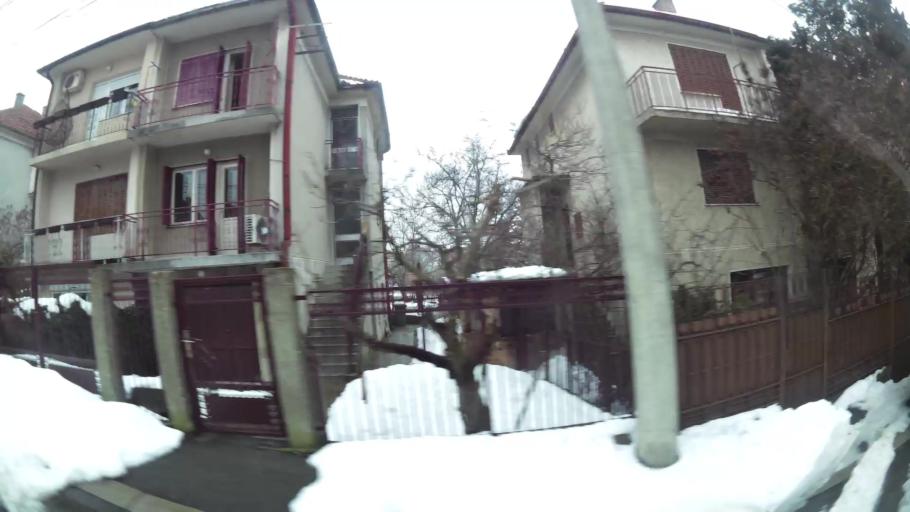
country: RS
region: Central Serbia
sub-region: Belgrade
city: Zvezdara
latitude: 44.7543
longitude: 20.5280
